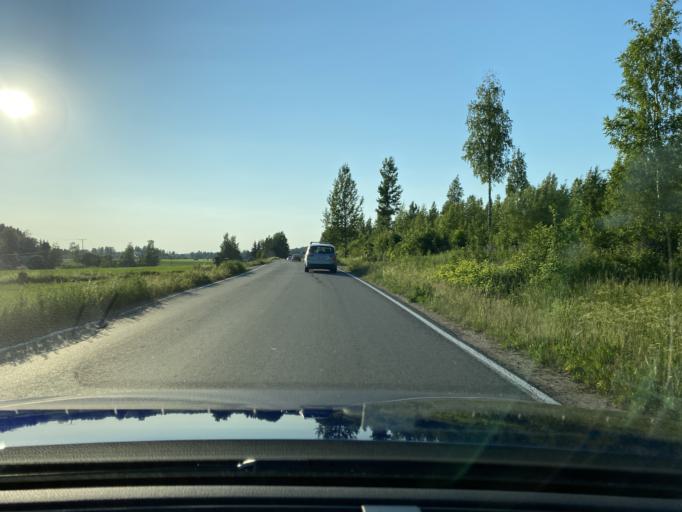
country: FI
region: Haeme
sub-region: Haemeenlinna
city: Tervakoski
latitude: 60.7304
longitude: 24.6737
